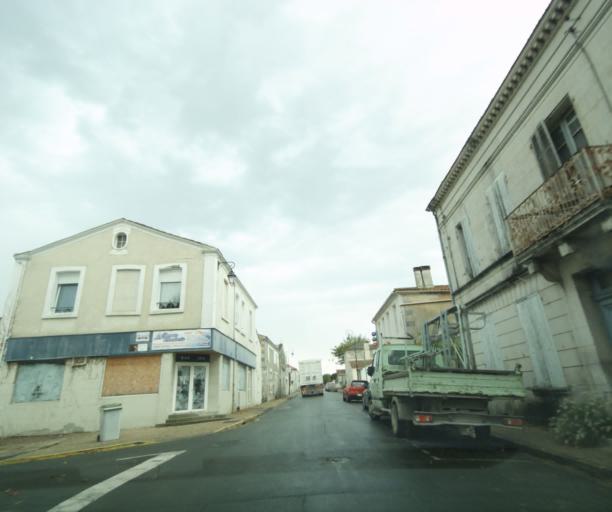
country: FR
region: Poitou-Charentes
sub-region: Departement de la Charente-Maritime
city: Tonnay-Charente
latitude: 45.9446
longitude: -0.8941
